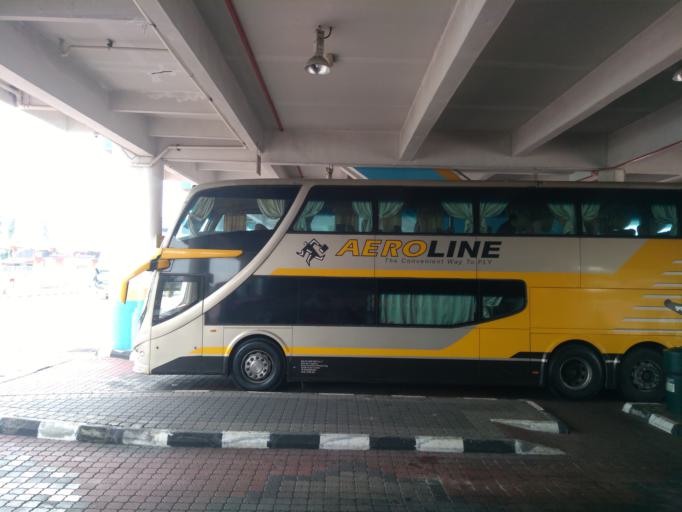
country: MY
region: Penang
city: Kampung Sungai Ara
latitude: 5.3434
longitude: 100.3005
